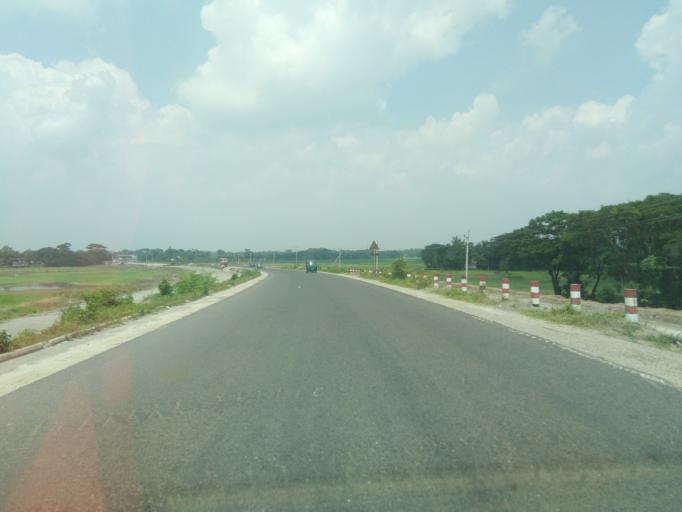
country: BD
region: Dhaka
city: Char Bhadrasan
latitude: 23.3837
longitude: 90.1254
